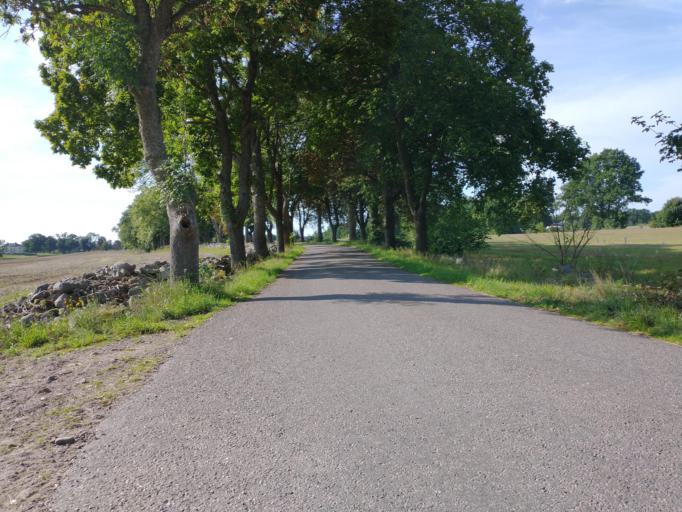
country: SE
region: Kalmar
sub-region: Kalmar Kommun
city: Lindsdal
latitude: 56.7839
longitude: 16.3210
